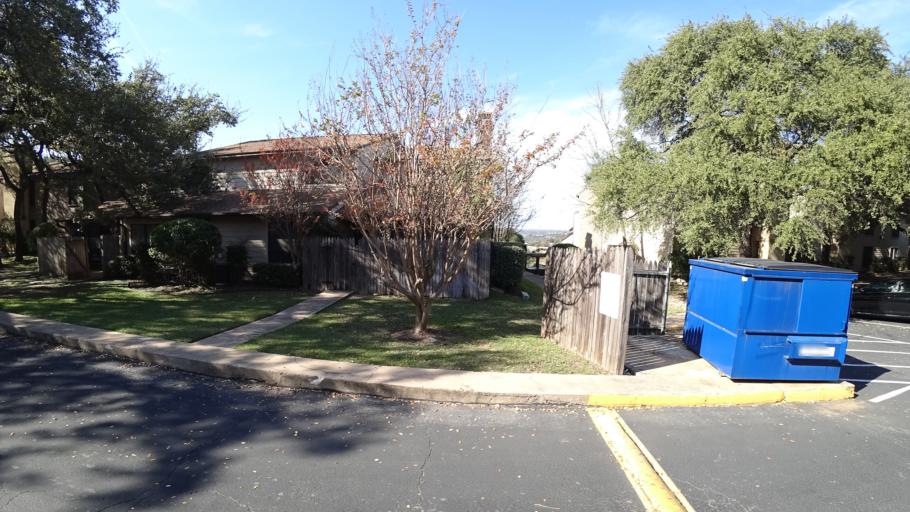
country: US
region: Texas
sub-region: Williamson County
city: Jollyville
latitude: 30.3754
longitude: -97.7586
